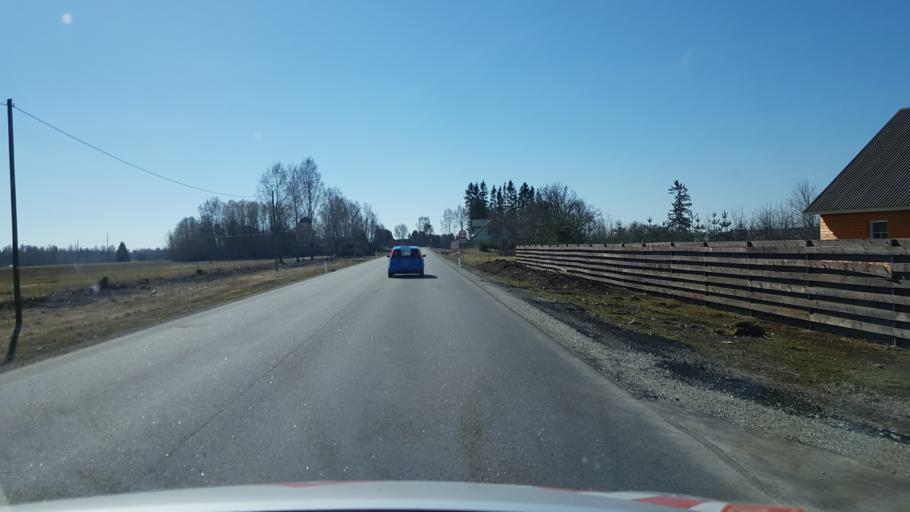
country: EE
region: Laeaene-Virumaa
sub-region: Vinni vald
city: Vinni
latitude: 59.1075
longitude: 26.6185
